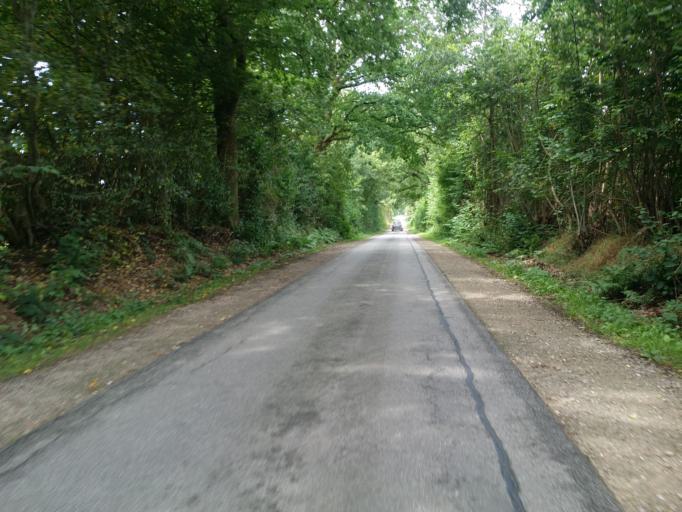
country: DE
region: Schleswig-Holstein
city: Huje
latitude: 53.9814
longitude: 9.4296
